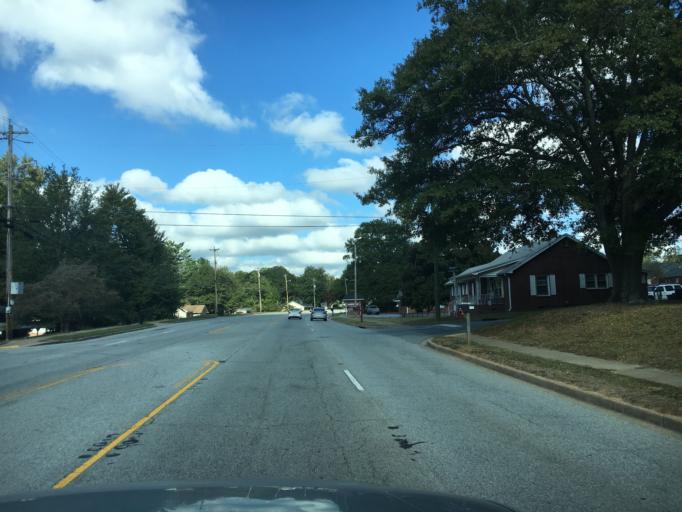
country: US
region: South Carolina
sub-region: Greenville County
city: Greer
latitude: 34.9245
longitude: -82.2194
